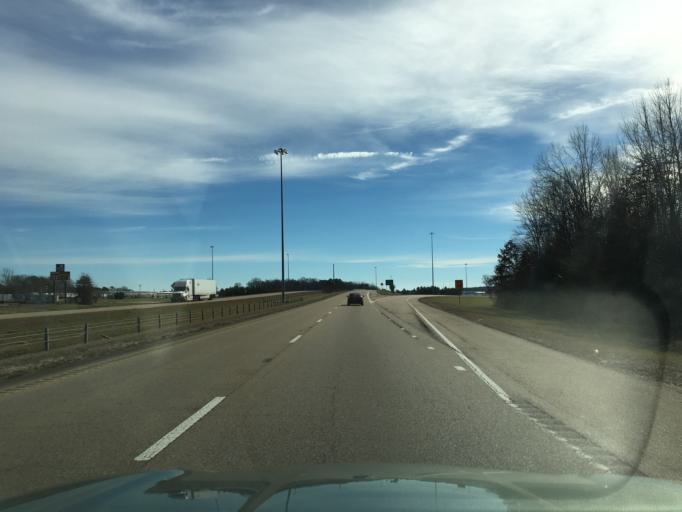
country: US
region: Mississippi
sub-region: Lee County
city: Saltillo
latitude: 34.3575
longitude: -88.8449
